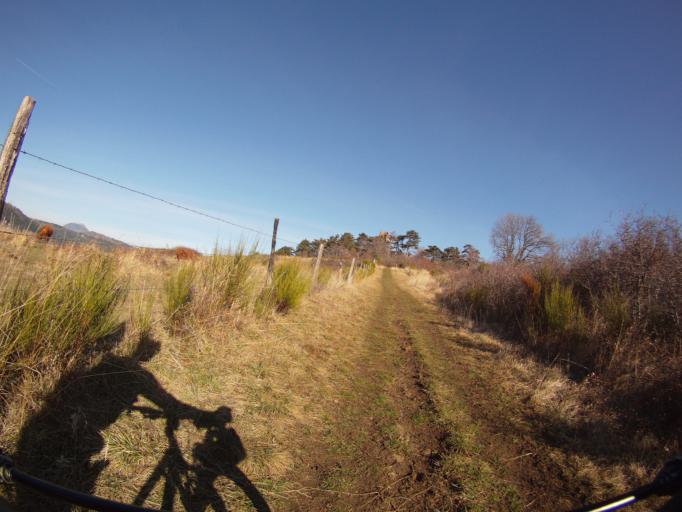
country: FR
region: Auvergne
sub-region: Departement du Puy-de-Dome
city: Ceyrat
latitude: 45.7298
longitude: 3.0760
